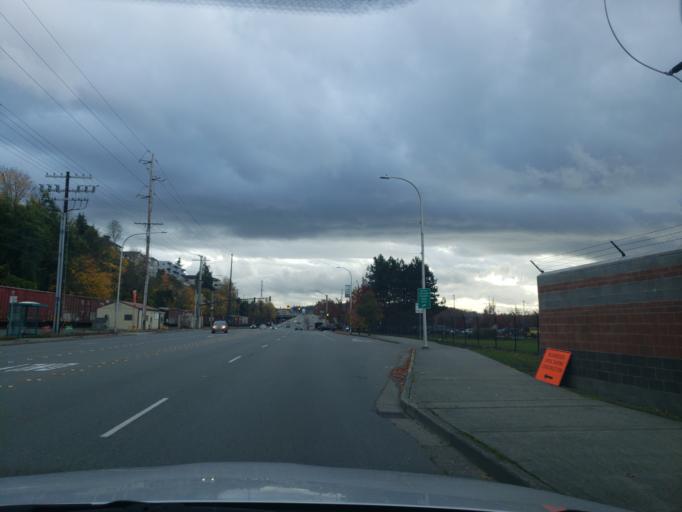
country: US
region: Washington
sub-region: Snohomish County
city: Everett
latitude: 47.9937
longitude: -122.2138
